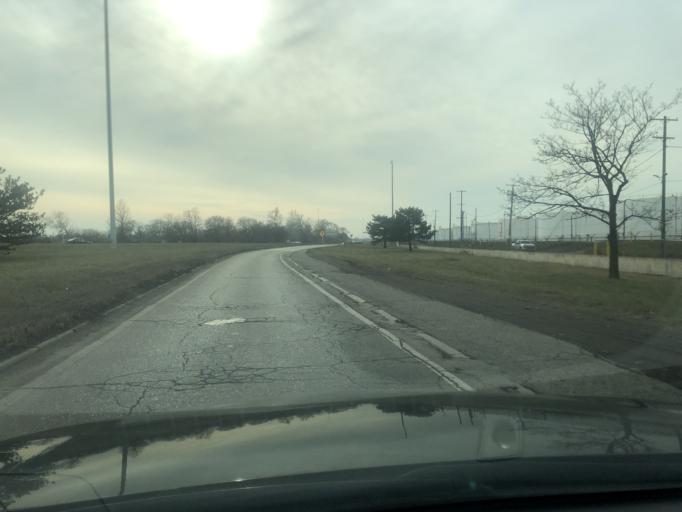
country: US
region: Michigan
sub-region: Wayne County
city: Melvindale
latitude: 42.2773
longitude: -83.1589
